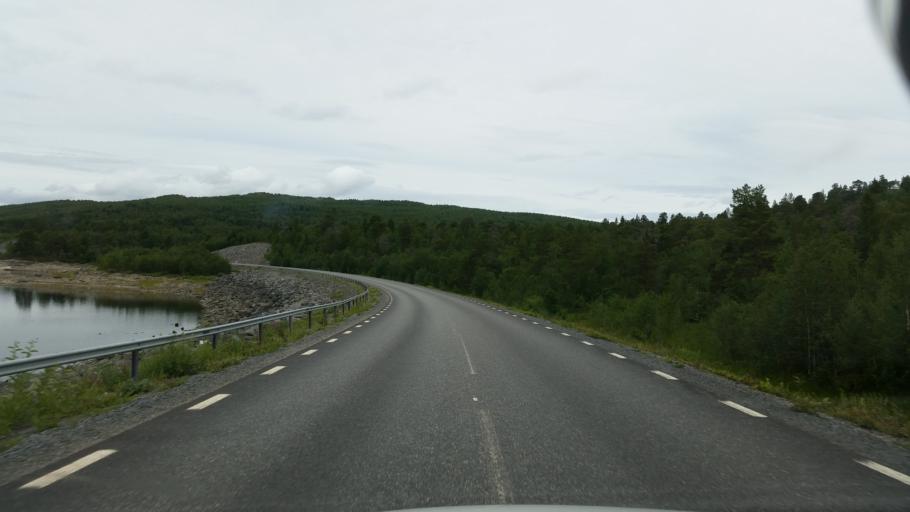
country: NO
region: Nordland
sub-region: Sorfold
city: Straumen
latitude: 66.5173
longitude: 16.4001
